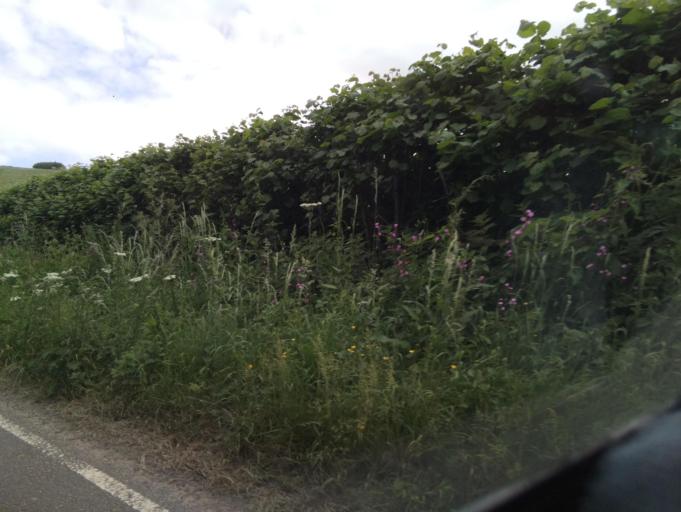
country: GB
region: England
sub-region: Dorset
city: Sherborne
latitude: 50.9904
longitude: -2.5033
